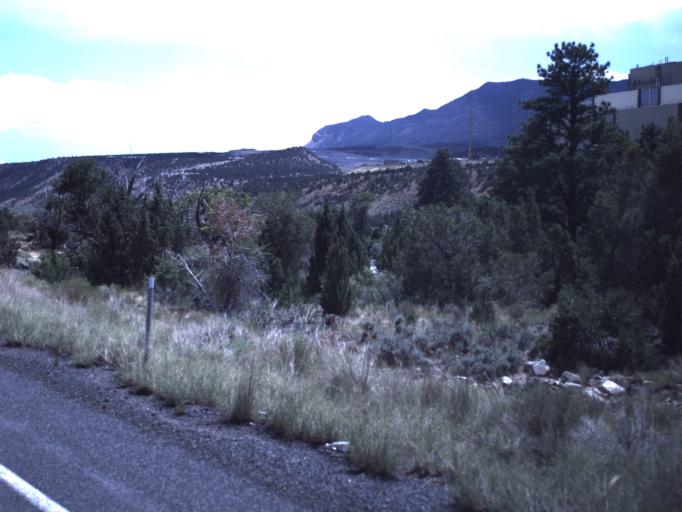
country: US
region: Utah
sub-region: Emery County
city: Huntington
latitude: 39.3851
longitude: -111.0772
